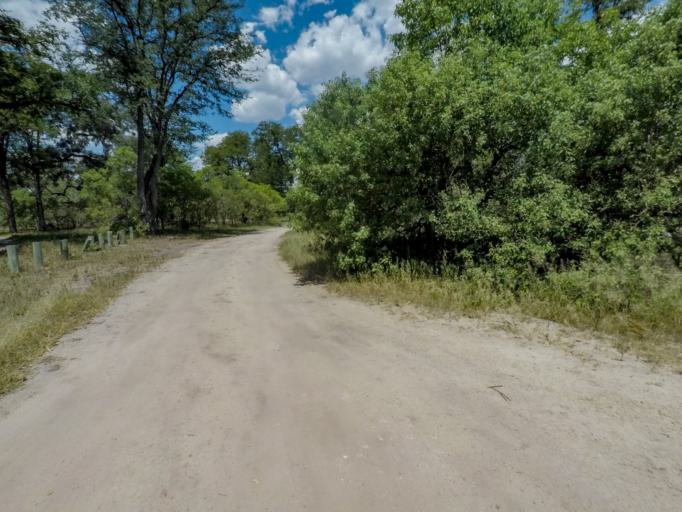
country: BW
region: North West
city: Maun
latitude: -19.1735
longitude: 23.7514
